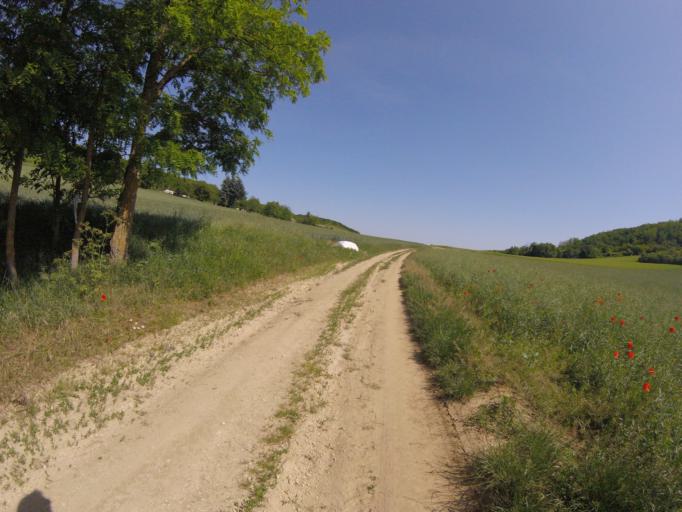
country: HU
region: Zala
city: Zalaszentgrot
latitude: 46.9096
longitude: 17.0548
